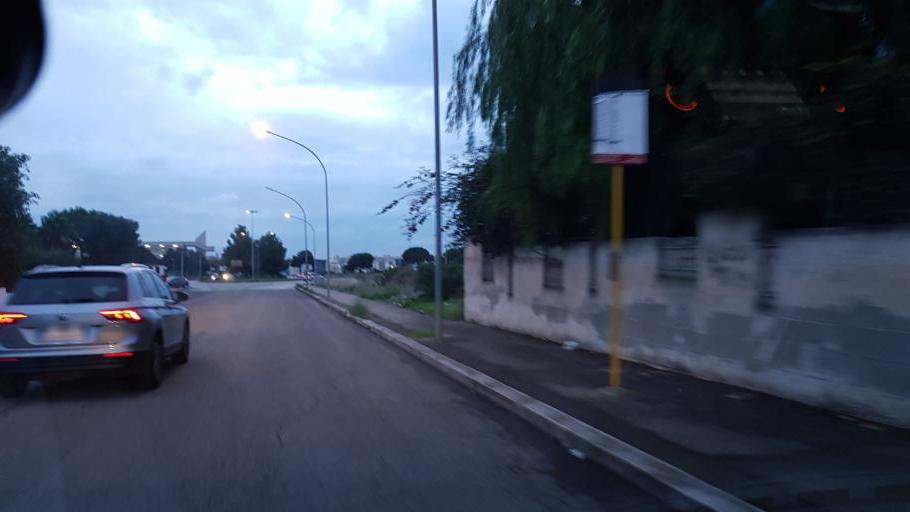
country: IT
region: Apulia
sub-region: Provincia di Taranto
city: Paolo VI
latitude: 40.5285
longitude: 17.2813
